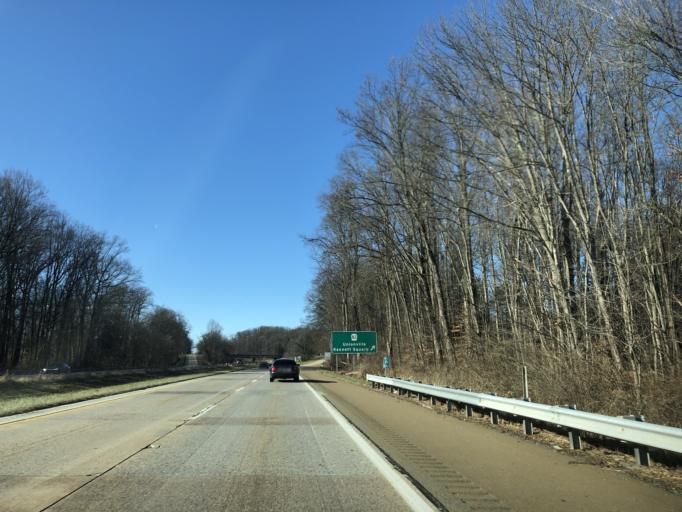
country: US
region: Pennsylvania
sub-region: Chester County
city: Kennett Square
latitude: 39.8566
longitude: -75.7091
